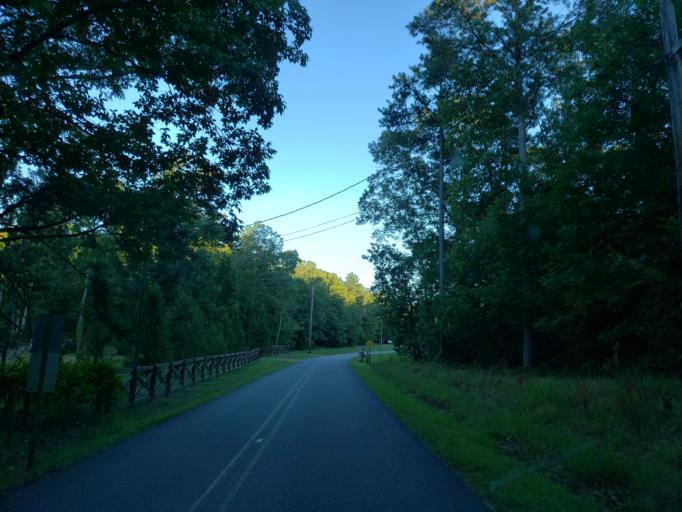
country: US
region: Georgia
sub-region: Bartow County
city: Euharlee
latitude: 34.0839
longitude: -84.9293
